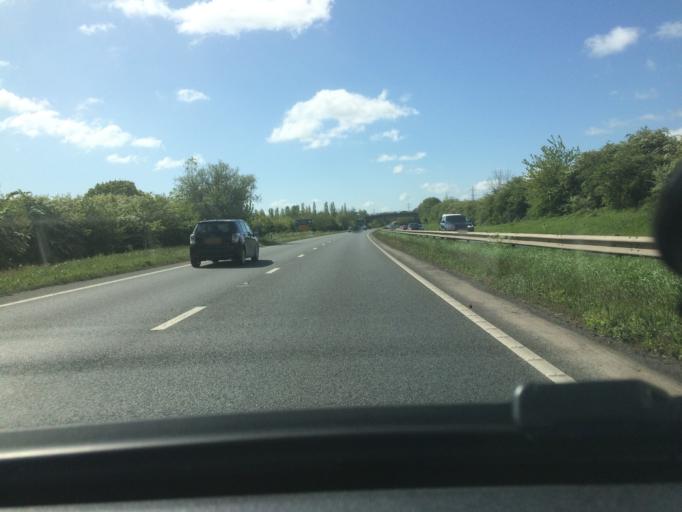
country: GB
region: Wales
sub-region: Wrexham
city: Ruabon
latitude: 53.0118
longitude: -3.0226
